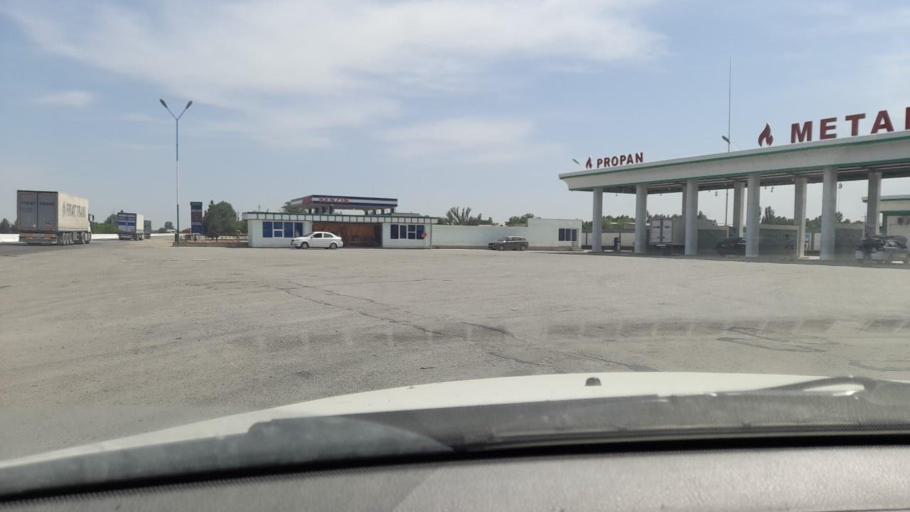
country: UZ
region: Navoiy
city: Navoiy
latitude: 40.0772
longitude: 65.6130
